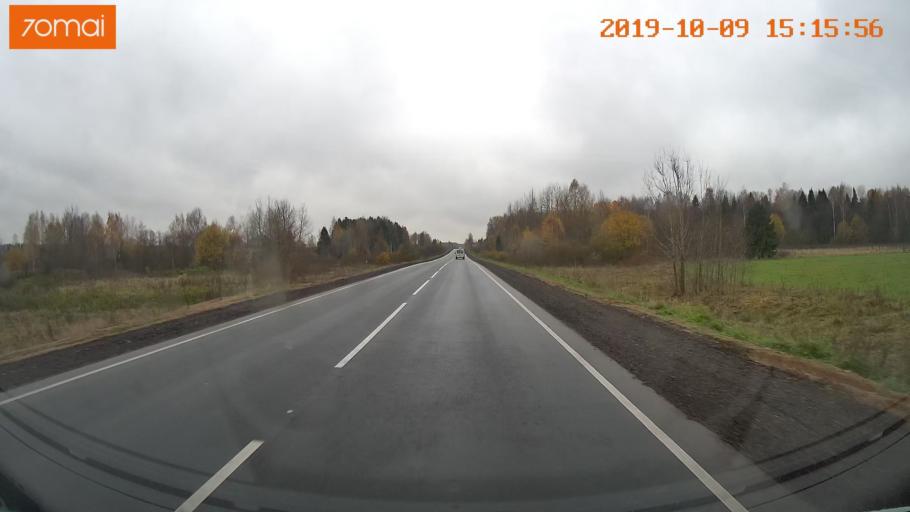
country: RU
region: Kostroma
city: Susanino
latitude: 58.1163
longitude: 41.5878
